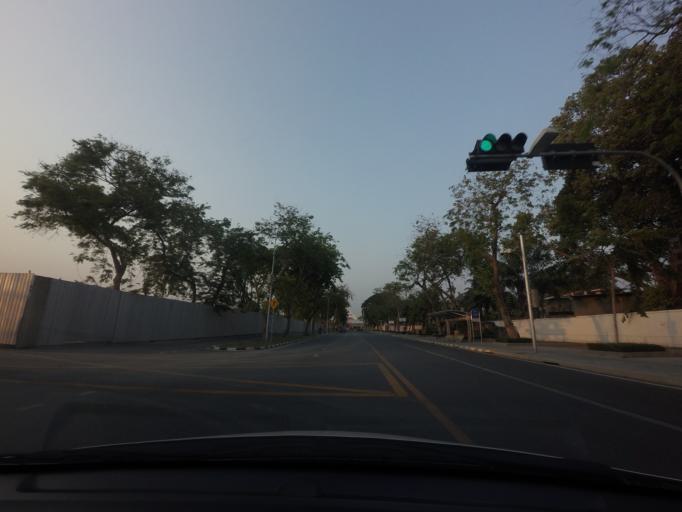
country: TH
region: Bangkok
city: Dusit
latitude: 13.7738
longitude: 100.5149
